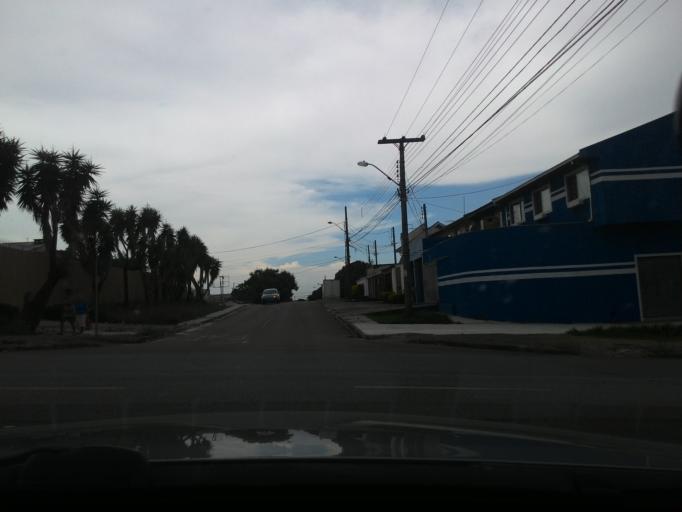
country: BR
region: Parana
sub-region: Pinhais
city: Pinhais
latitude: -25.4450
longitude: -49.2215
